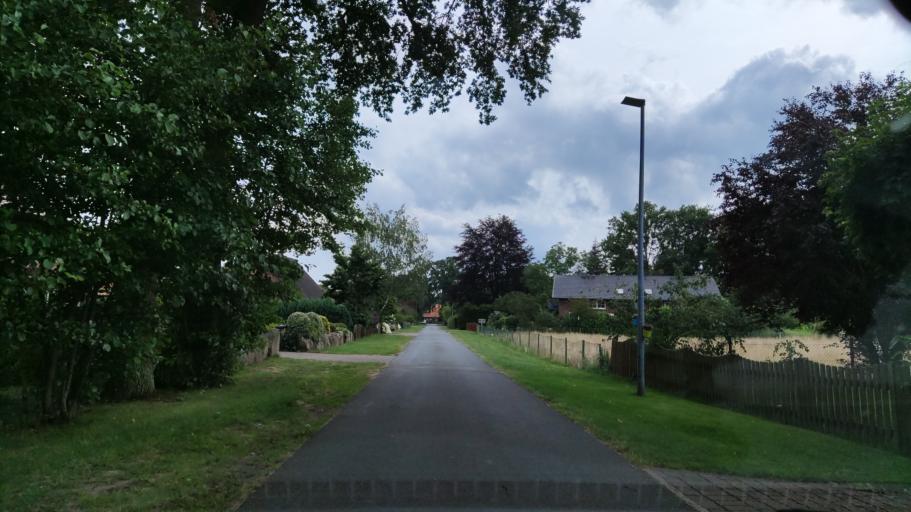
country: DE
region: Lower Saxony
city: Damnatz
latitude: 53.0976
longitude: 11.1440
